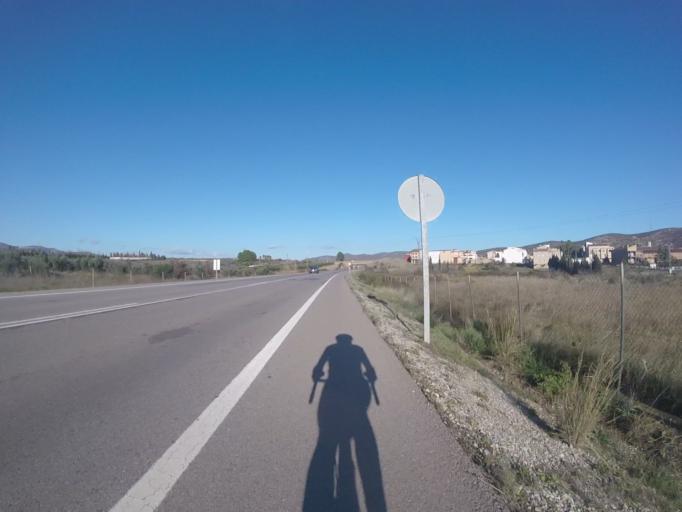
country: ES
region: Valencia
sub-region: Provincia de Castello
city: Cuevas de Vinroma
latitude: 40.3094
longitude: 0.1151
